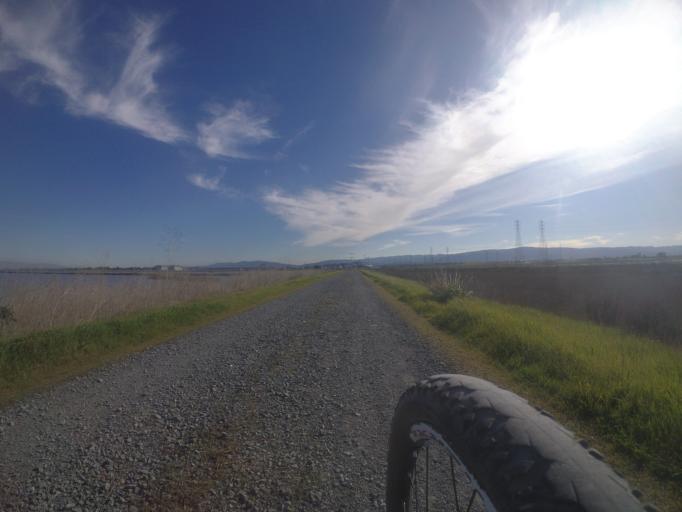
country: US
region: California
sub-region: Santa Clara County
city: Mountain View
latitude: 37.4395
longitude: -122.0680
